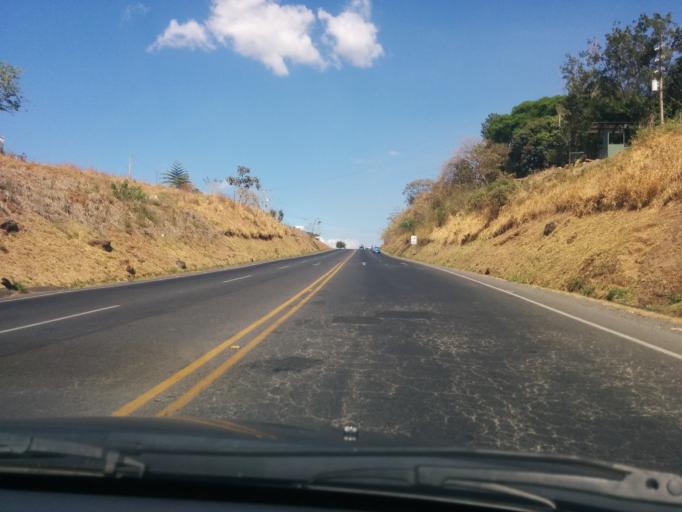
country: CR
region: Alajuela
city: Atenas
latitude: 10.0154
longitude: -84.3493
